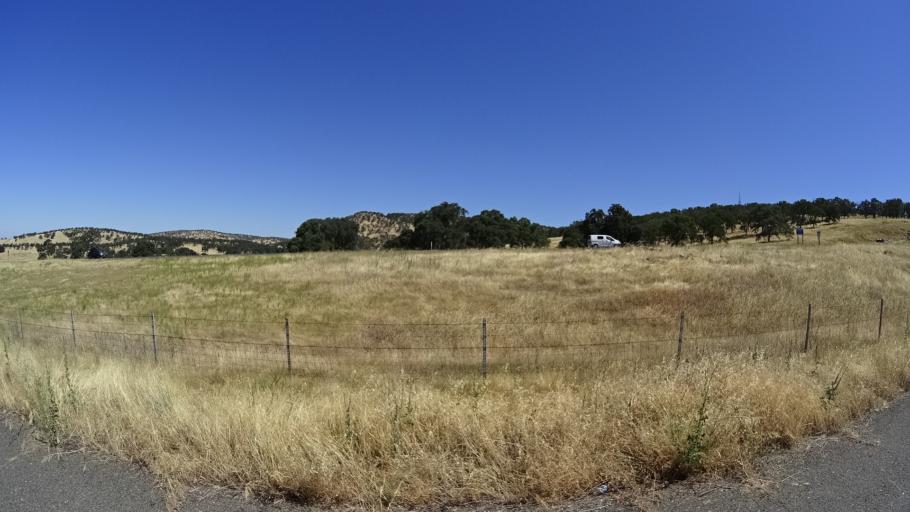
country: US
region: California
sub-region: Calaveras County
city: Copperopolis
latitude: 37.9420
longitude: -120.7162
